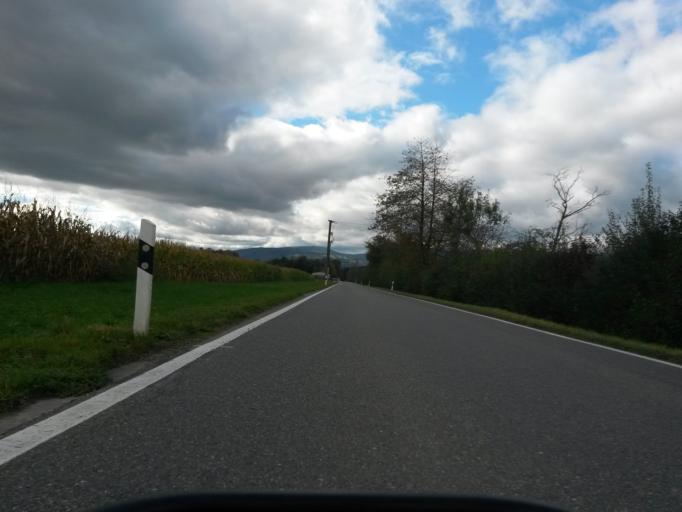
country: CH
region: Bern
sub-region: Biel/Bienne District
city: Meinisberg
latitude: 47.1419
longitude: 7.3550
